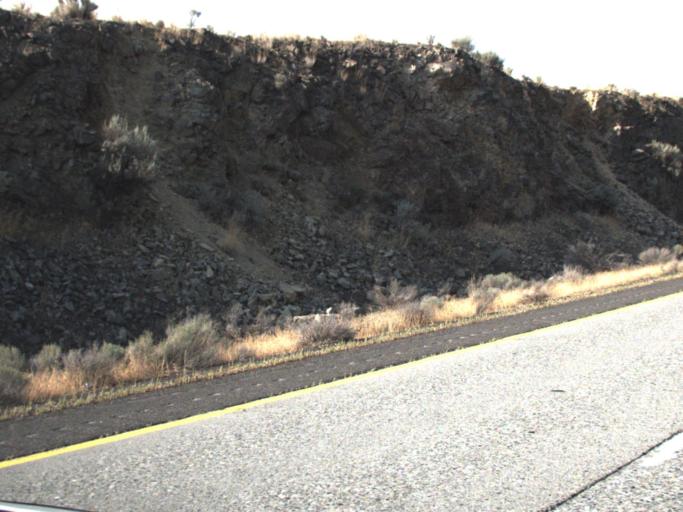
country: US
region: Washington
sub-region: Yakima County
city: Terrace Heights
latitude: 46.7129
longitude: -120.4276
